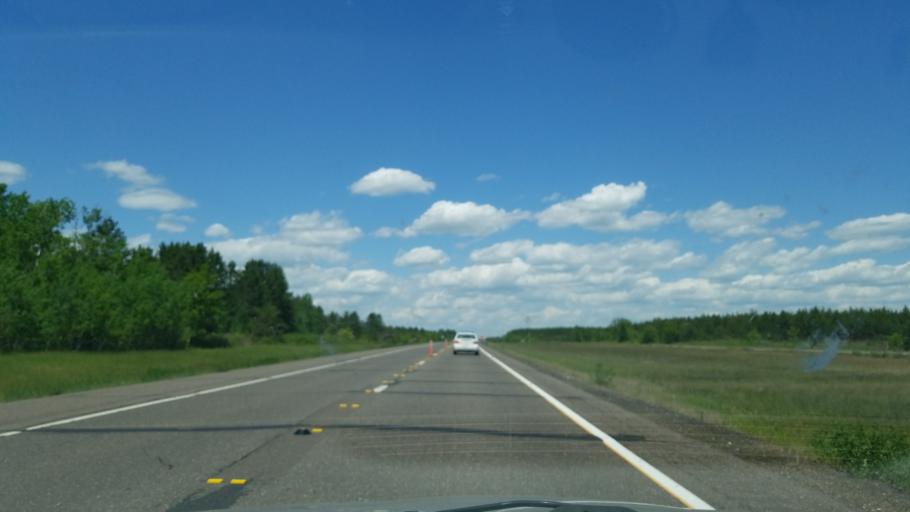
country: US
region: Minnesota
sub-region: Carlton County
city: Moose Lake
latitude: 46.3338
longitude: -92.8197
